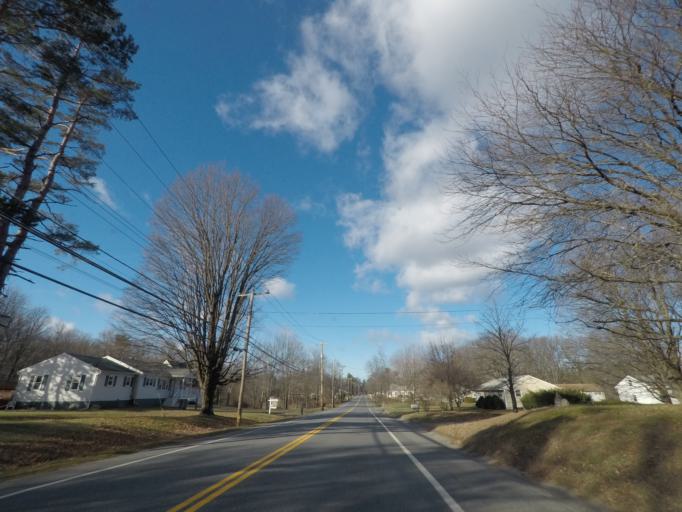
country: US
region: New York
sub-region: Saratoga County
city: Waterford
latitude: 42.8350
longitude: -73.7301
